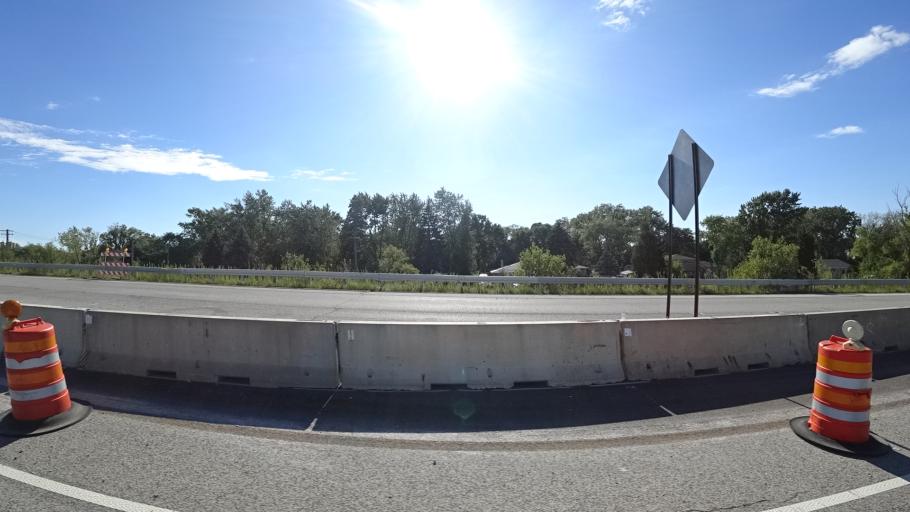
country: US
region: Illinois
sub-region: Cook County
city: Oak Forest
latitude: 41.5836
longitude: -87.7352
